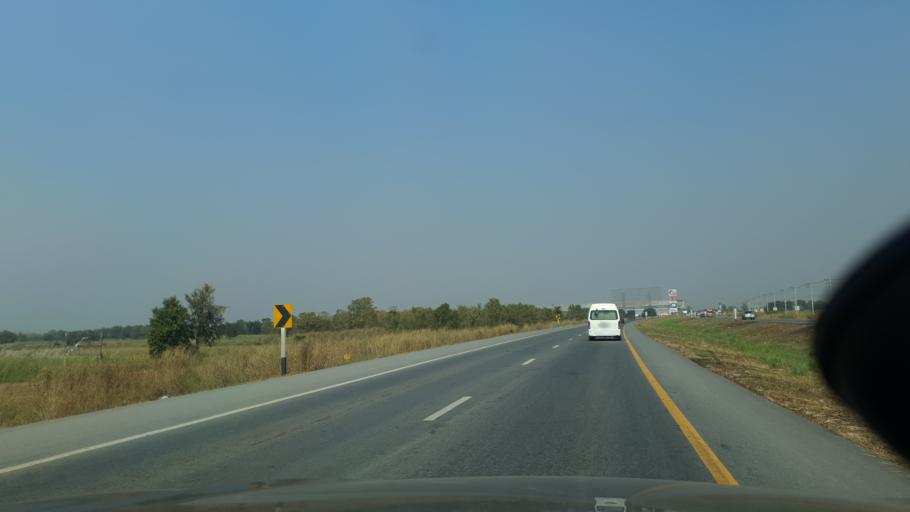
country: TH
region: Nakhon Sawan
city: Nakhon Sawan
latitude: 15.6773
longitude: 100.0565
